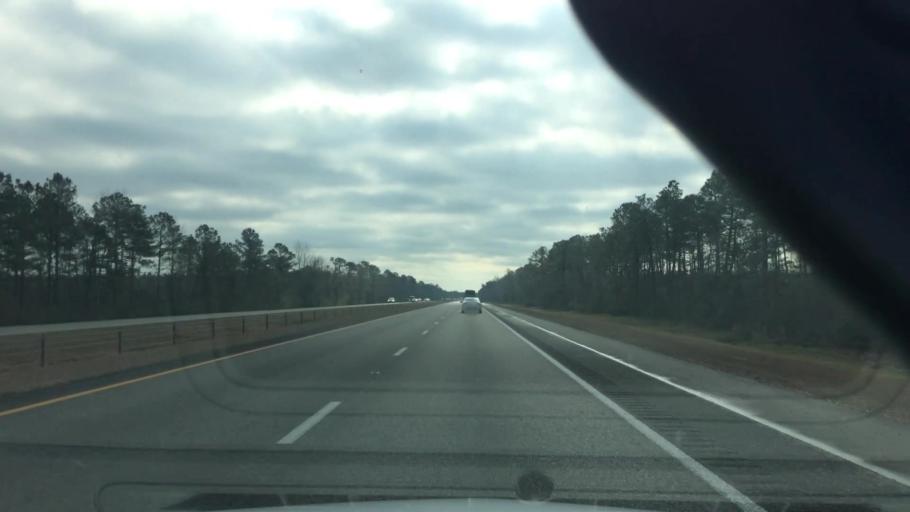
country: US
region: North Carolina
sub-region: Pender County
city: Rocky Point
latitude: 34.4086
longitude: -77.8711
